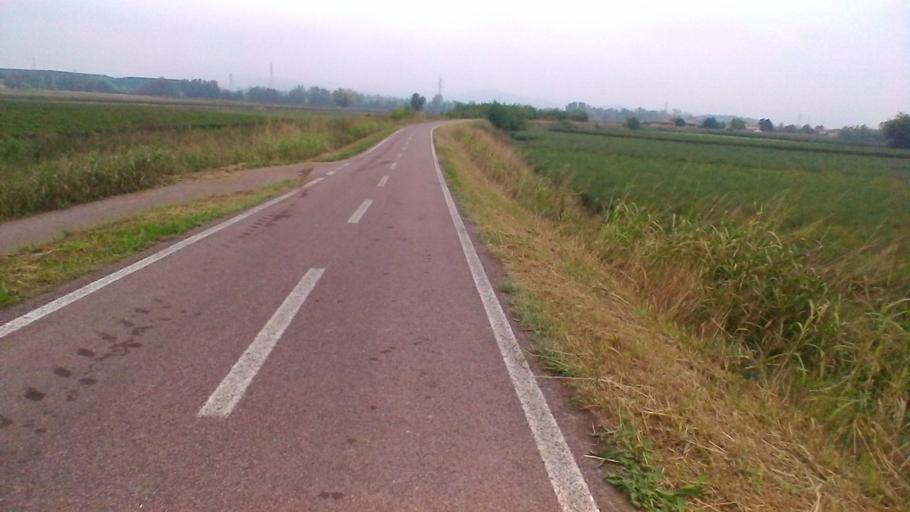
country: IT
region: Veneto
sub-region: Provincia di Verona
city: Campagnola
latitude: 45.3879
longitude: 11.0720
